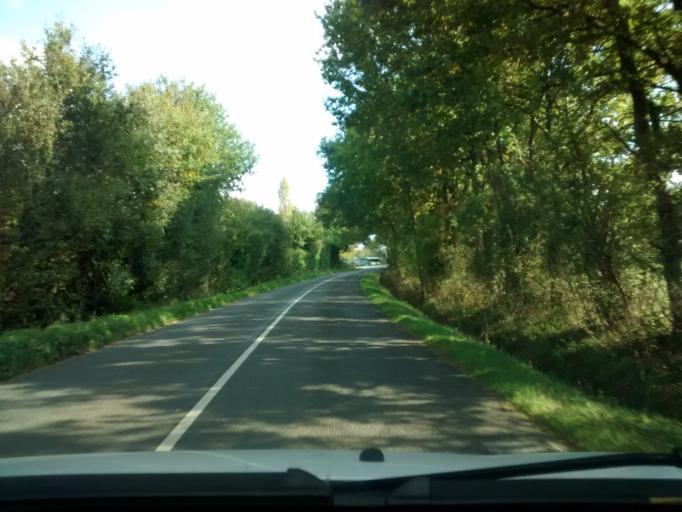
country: FR
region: Pays de la Loire
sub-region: Departement de la Loire-Atlantique
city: Orvault
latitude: 47.2801
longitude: -1.6419
